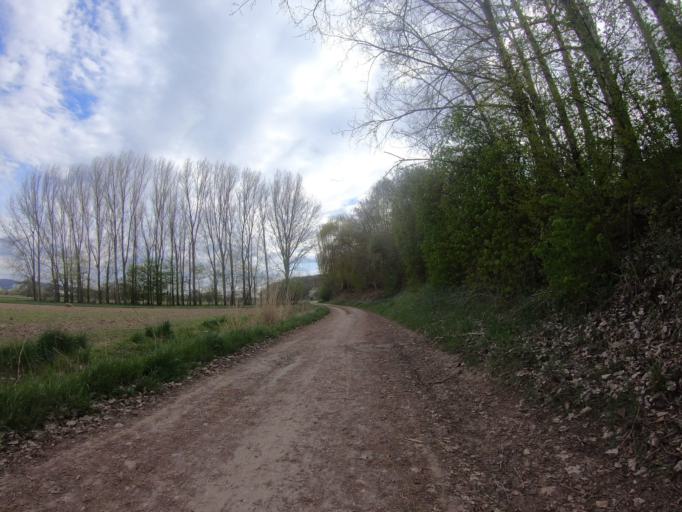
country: DE
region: Lower Saxony
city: Nordstemmen
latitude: 52.1816
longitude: 9.7768
